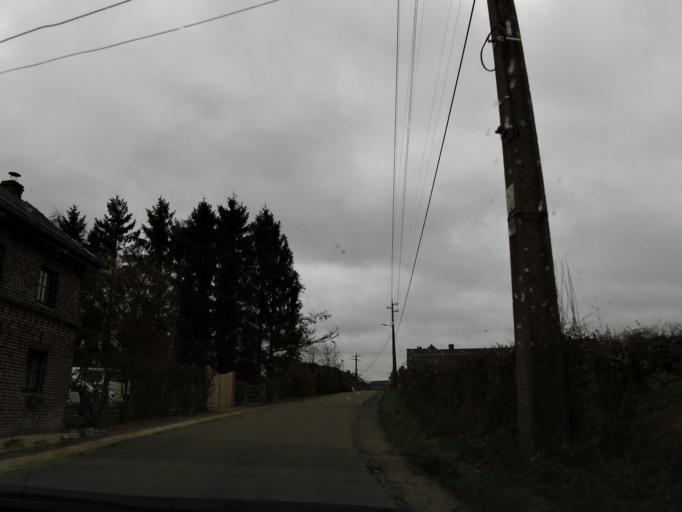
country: BE
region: Flanders
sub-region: Provincie Limburg
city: Sint-Pieters-Voeren
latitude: 50.7553
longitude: 5.8698
